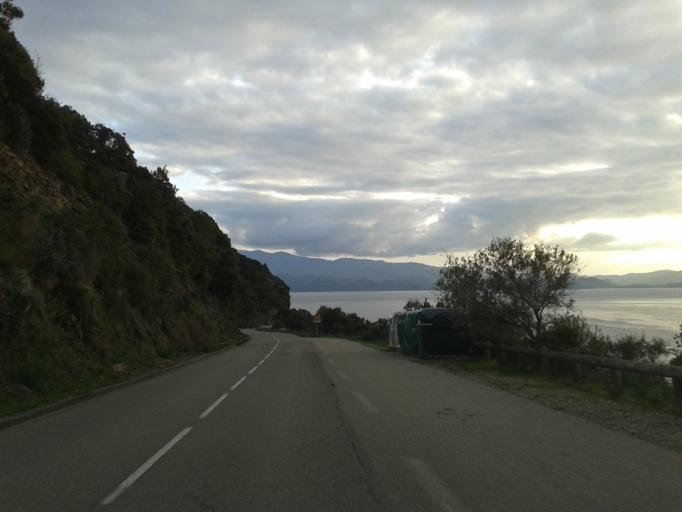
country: FR
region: Corsica
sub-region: Departement de la Haute-Corse
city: Saint-Florent
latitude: 42.7669
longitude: 9.3399
